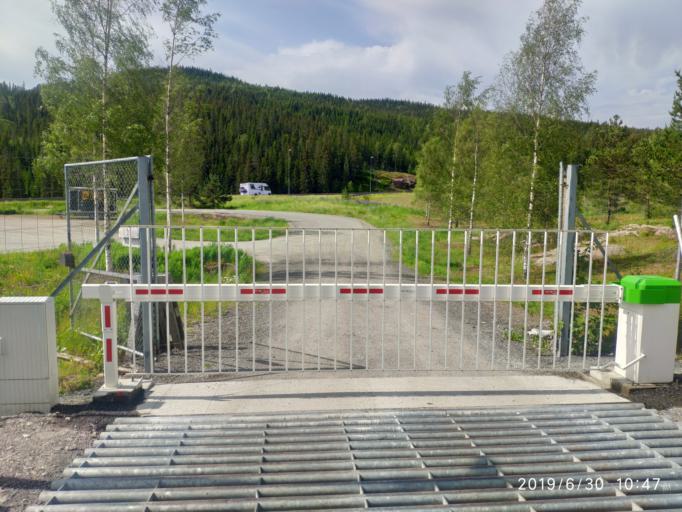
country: NO
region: Oppland
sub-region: Lunner
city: Grua
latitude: 60.2760
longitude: 10.7465
